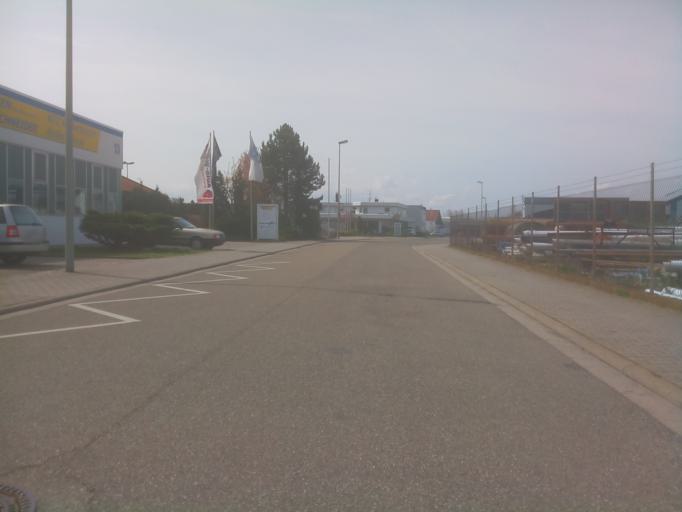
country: DE
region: Hesse
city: Lampertheim
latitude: 49.5963
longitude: 8.4892
